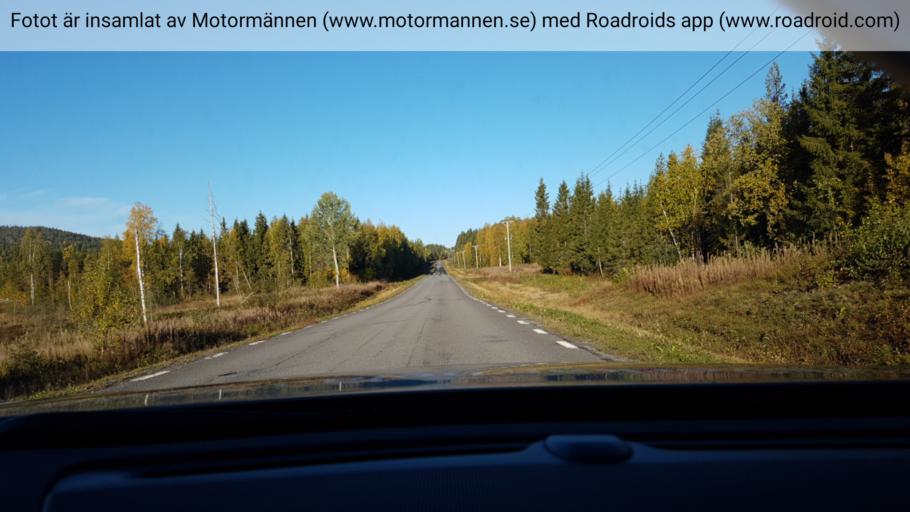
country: SE
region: Norrbotten
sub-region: Bodens Kommun
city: Boden
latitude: 65.9486
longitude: 21.6250
